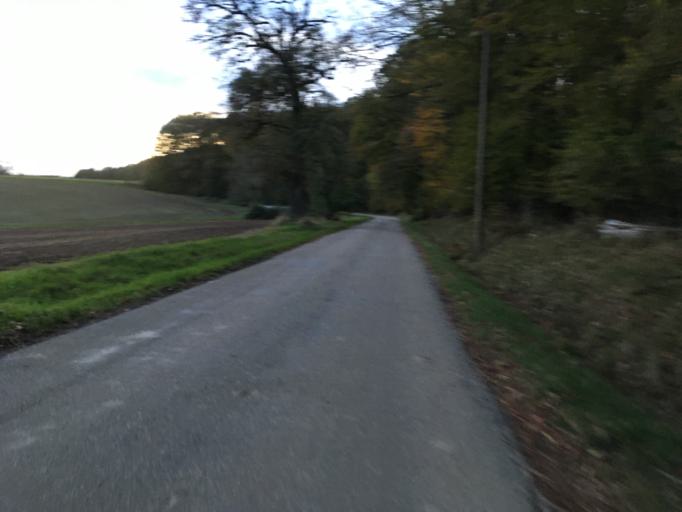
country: DE
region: Baden-Wuerttemberg
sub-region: Karlsruhe Region
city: Osterburken
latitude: 49.3922
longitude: 9.4564
